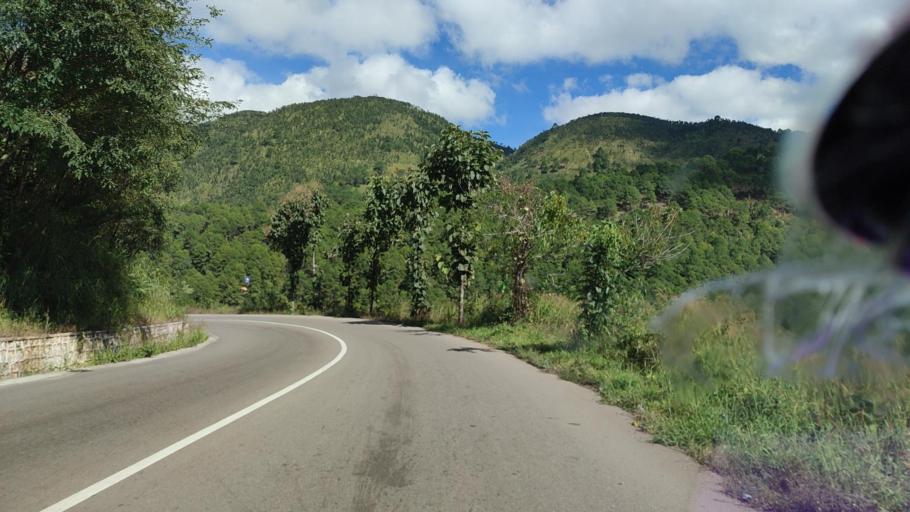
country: MM
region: Mandalay
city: Yamethin
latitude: 20.6488
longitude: 96.5540
